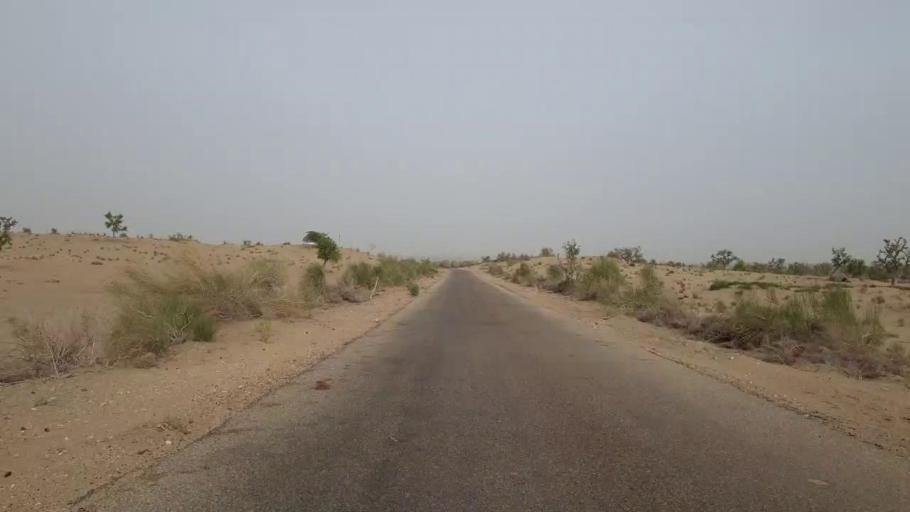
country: PK
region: Sindh
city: Islamkot
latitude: 24.5516
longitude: 70.3536
